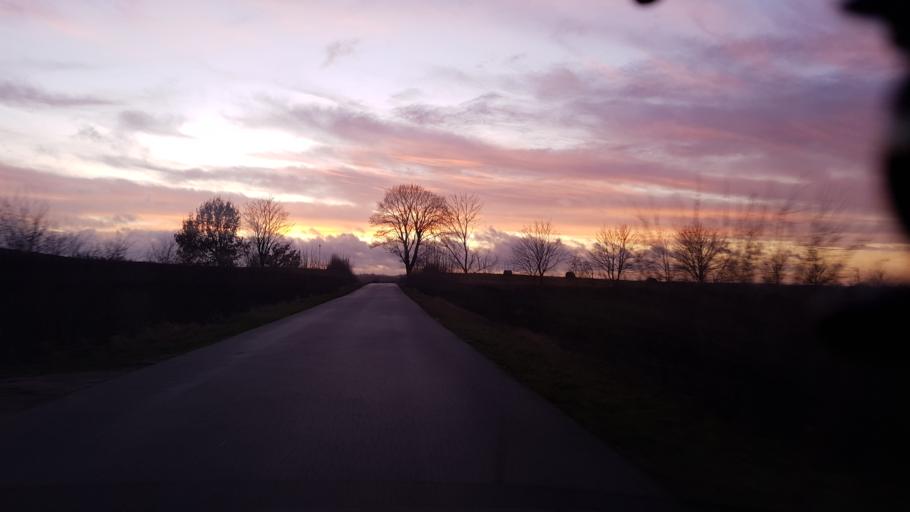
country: PL
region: Pomeranian Voivodeship
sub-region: Powiat bytowski
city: Tuchomie
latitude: 54.1296
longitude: 17.3532
